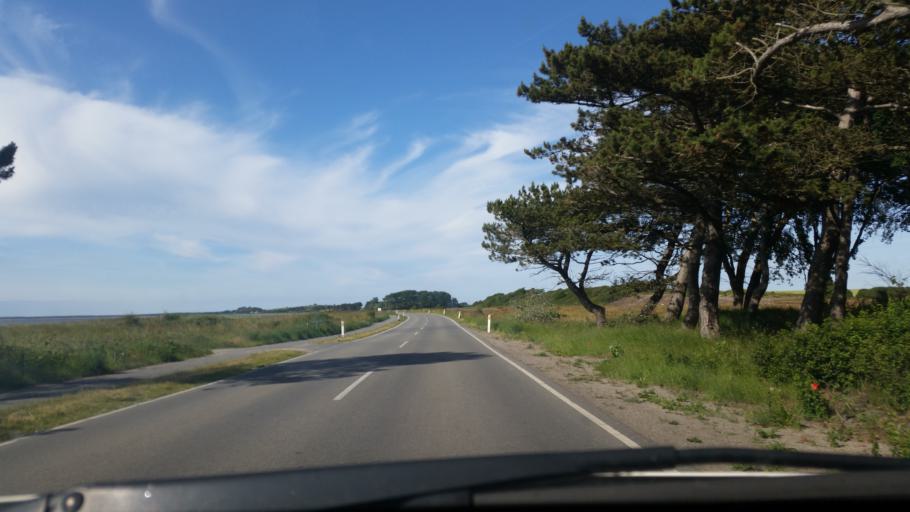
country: DK
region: Central Jutland
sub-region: Samso Kommune
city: Tranebjerg
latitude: 55.8672
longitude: 10.5833
